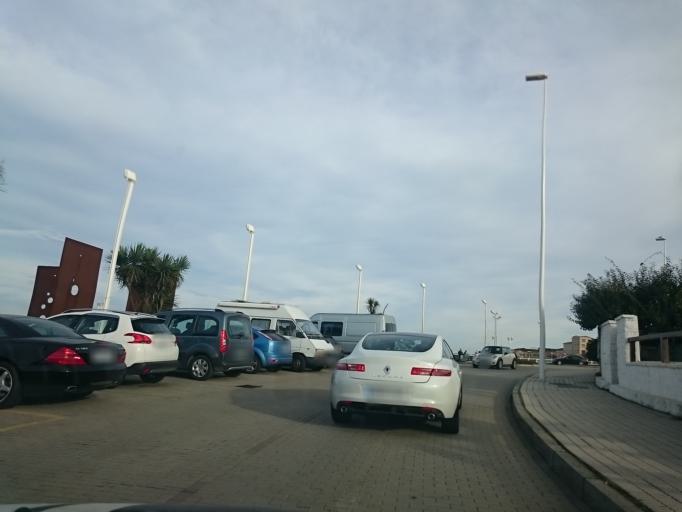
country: ES
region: Asturias
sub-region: Province of Asturias
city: Gijon
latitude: 43.5446
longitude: -5.6081
